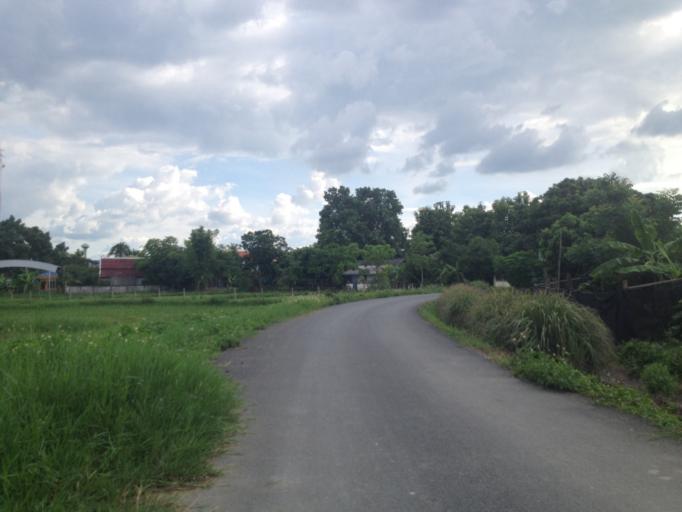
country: TH
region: Chiang Mai
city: Hang Dong
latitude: 18.7162
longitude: 98.9305
